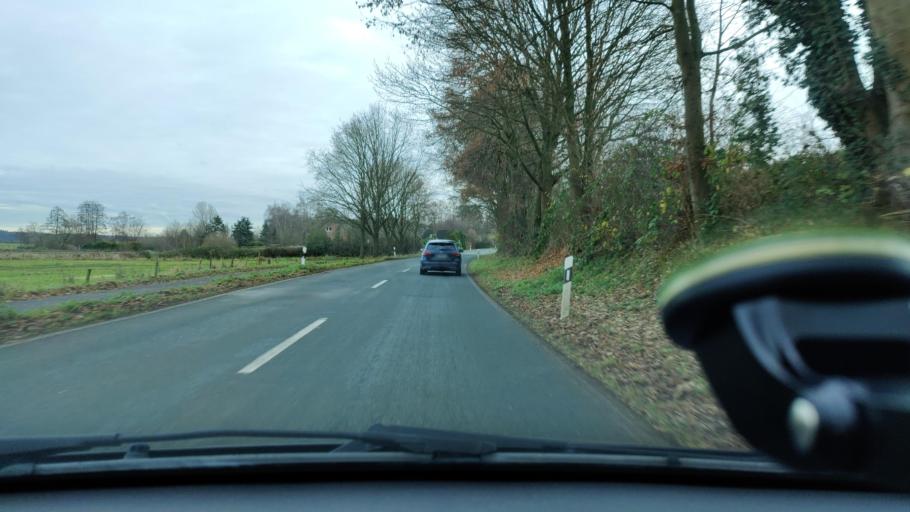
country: DE
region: North Rhine-Westphalia
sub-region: Regierungsbezirk Dusseldorf
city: Sonsbeck
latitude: 51.6287
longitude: 6.4138
